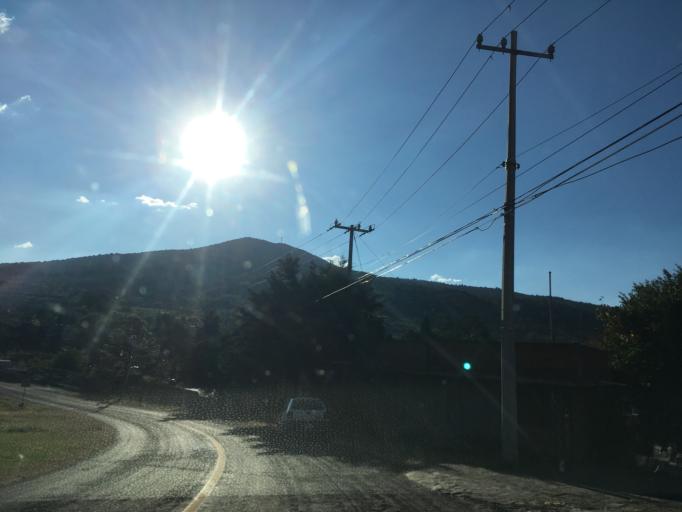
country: MX
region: Michoacan
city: Tzintzuntzan
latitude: 19.6251
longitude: -101.5752
